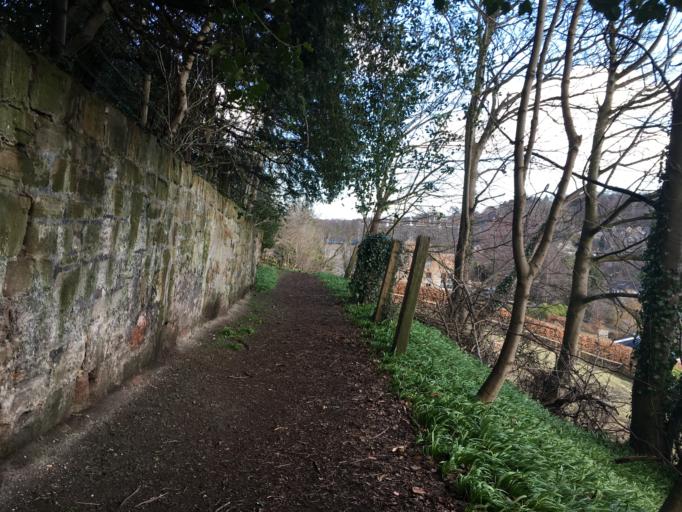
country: GB
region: Scotland
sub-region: Midlothian
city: Bonnyrigg
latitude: 55.8819
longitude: -3.1189
